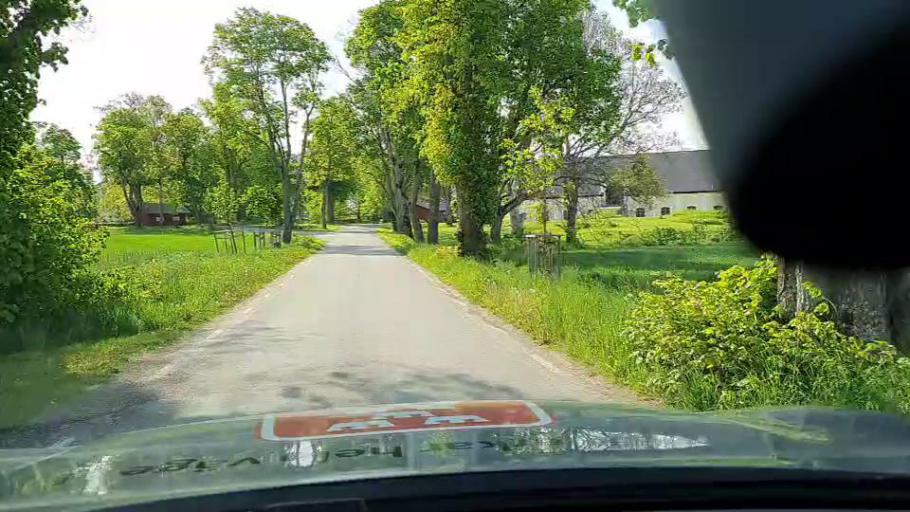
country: SE
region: Soedermanland
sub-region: Eskilstuna Kommun
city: Arla
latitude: 59.2587
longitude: 16.6540
